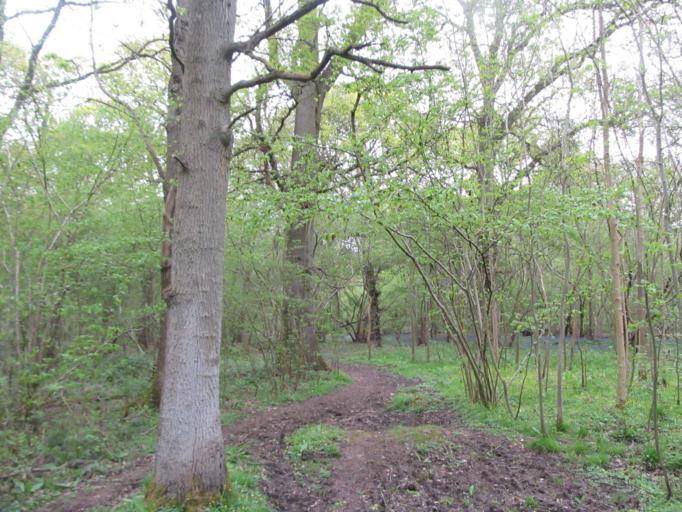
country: GB
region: England
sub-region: Royal Borough of Windsor and Maidenhead
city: Bisham
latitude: 51.5462
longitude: -0.7693
